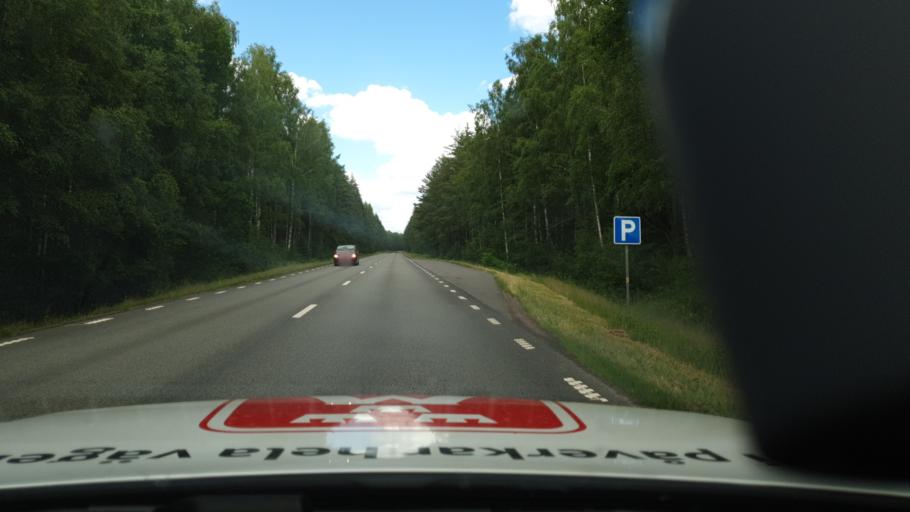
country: SE
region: Vaestra Goetaland
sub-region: Karlsborgs Kommun
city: Molltorp
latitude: 58.3984
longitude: 14.3581
